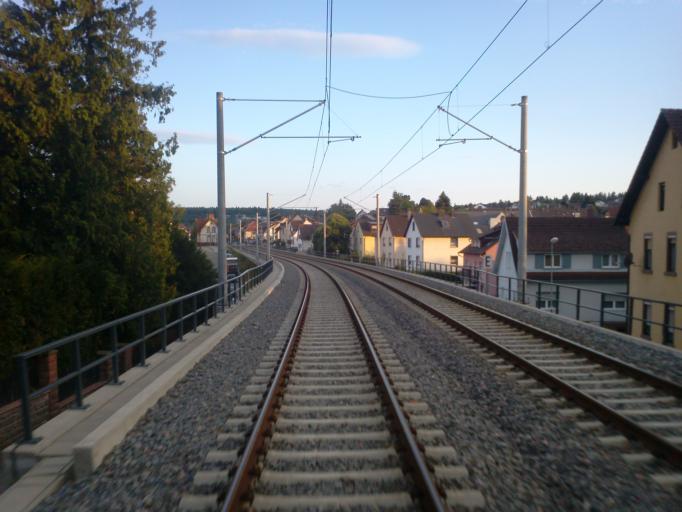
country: DE
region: Baden-Wuerttemberg
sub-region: Karlsruhe Region
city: Ettlingen
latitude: 48.9175
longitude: 8.5031
